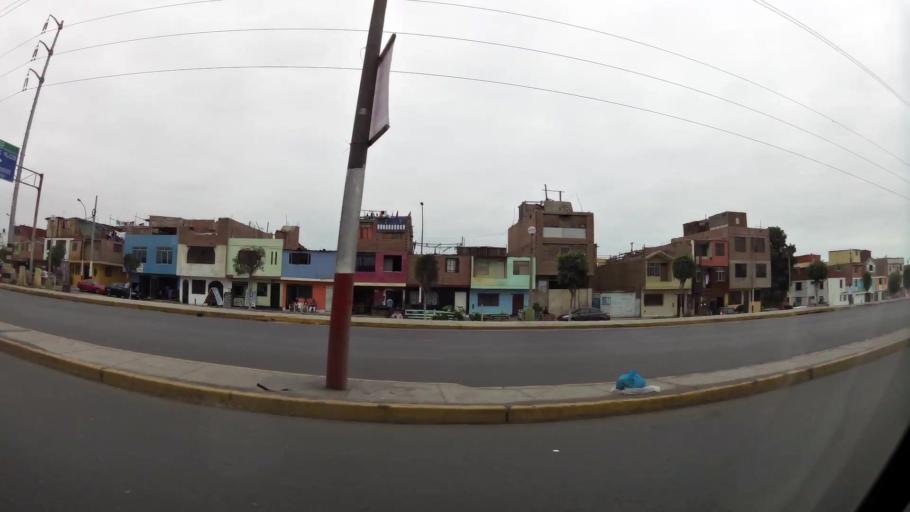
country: PE
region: Callao
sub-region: Callao
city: Callao
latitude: -12.0508
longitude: -77.1271
